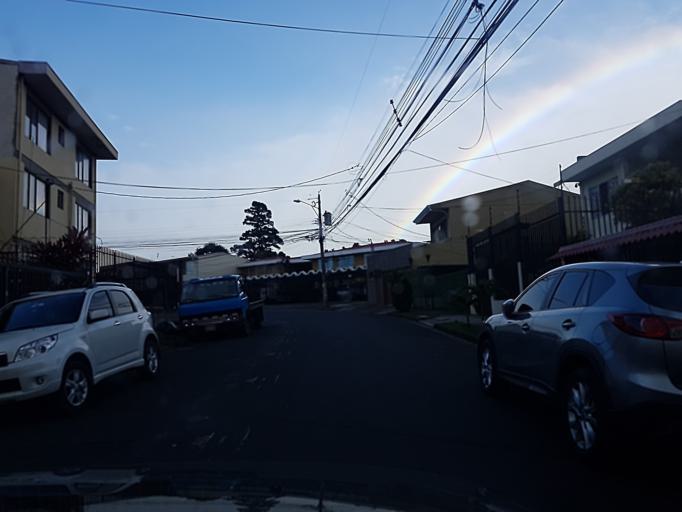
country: CR
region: San Jose
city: San Pedro
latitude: 9.9277
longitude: -84.0467
